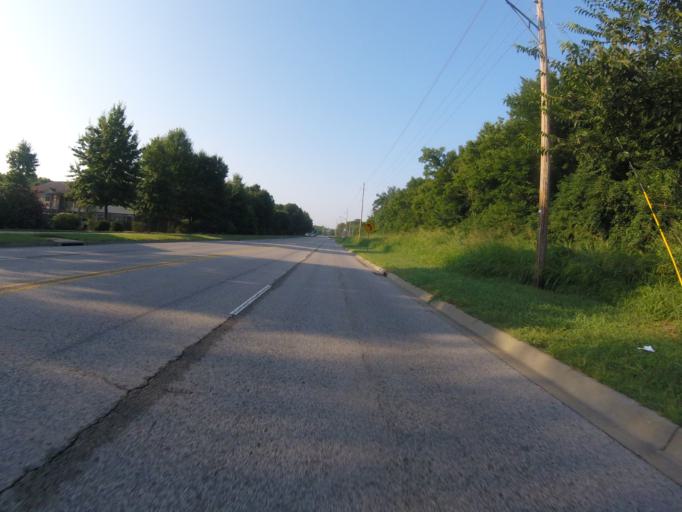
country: US
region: Arkansas
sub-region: Washington County
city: Johnson
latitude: 36.1055
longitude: -94.1636
